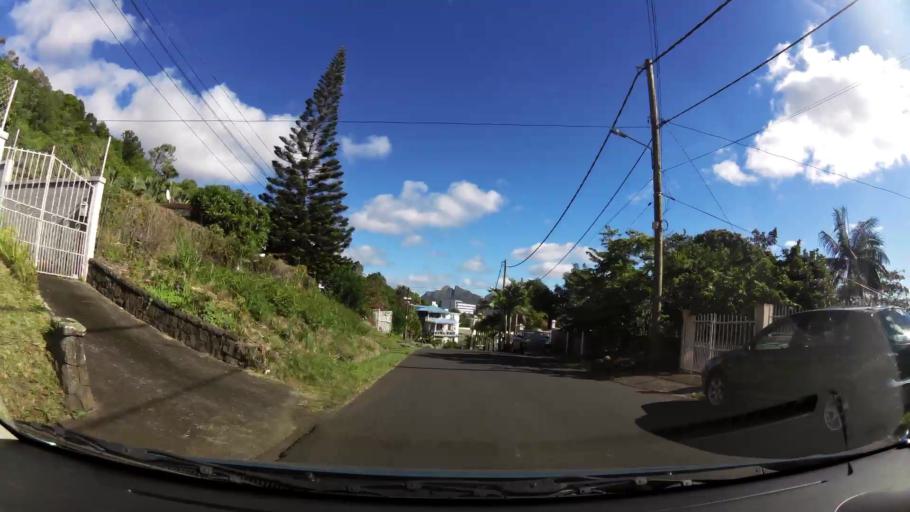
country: MU
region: Plaines Wilhems
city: Quatre Bornes
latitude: -20.2755
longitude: 57.4798
